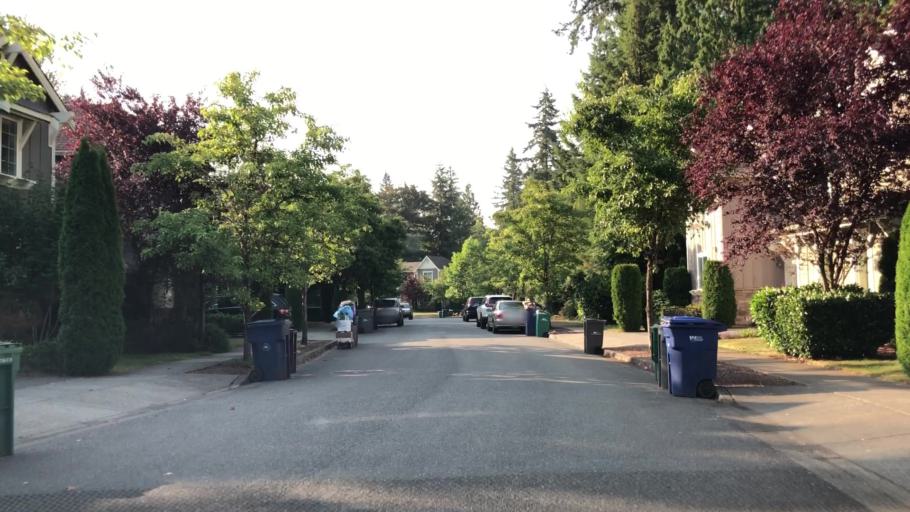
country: US
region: Washington
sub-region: King County
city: Union Hill-Novelty Hill
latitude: 47.6763
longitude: -122.0283
